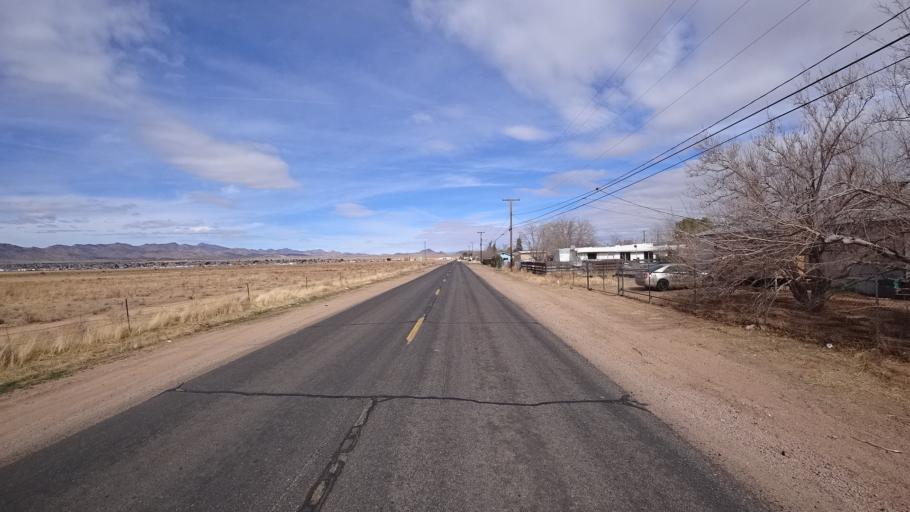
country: US
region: Arizona
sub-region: Mohave County
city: New Kingman-Butler
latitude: 35.2454
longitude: -113.9938
